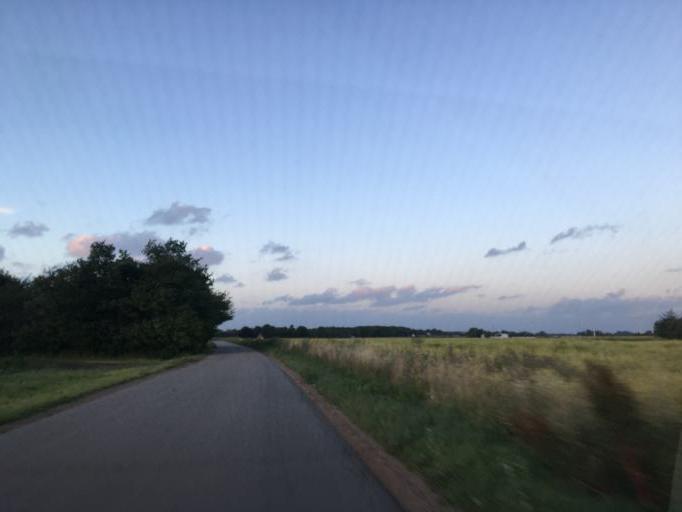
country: DK
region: Zealand
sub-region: Koge Kommune
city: Ejby
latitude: 55.5194
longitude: 12.0814
